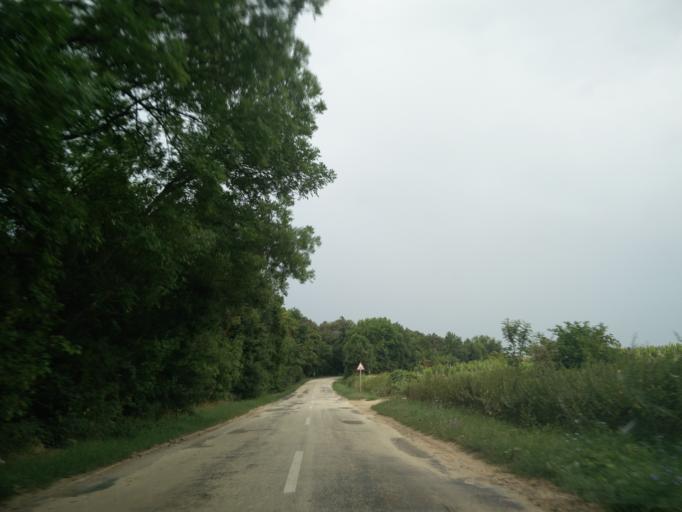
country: HU
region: Fejer
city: Etyek
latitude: 47.4419
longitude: 18.7033
